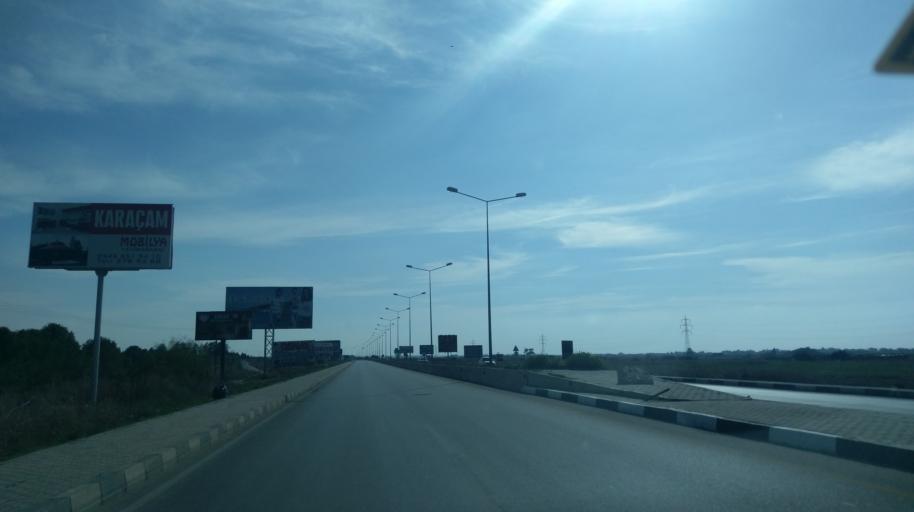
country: CY
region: Ammochostos
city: Famagusta
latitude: 35.1839
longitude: 33.8949
